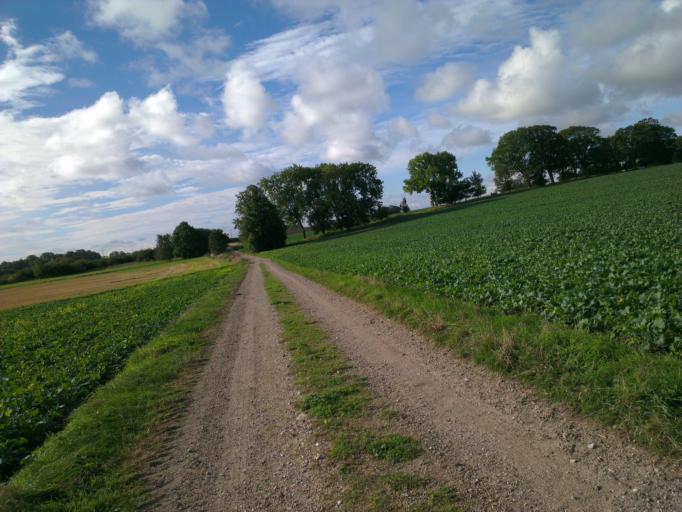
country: DK
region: Capital Region
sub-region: Frederikssund Kommune
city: Frederikssund
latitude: 55.8089
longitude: 12.0866
